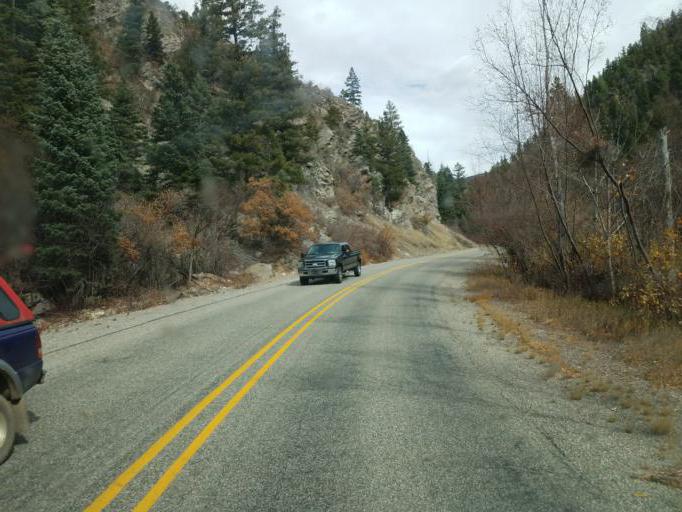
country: US
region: New Mexico
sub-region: Taos County
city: Arroyo Seco
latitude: 36.5654
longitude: -105.5252
